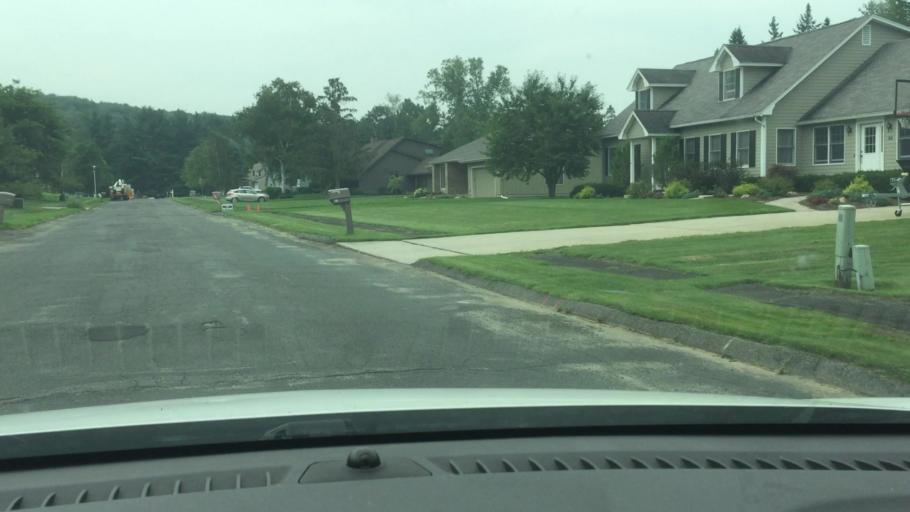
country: US
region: Massachusetts
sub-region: Berkshire County
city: Pittsfield
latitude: 42.4296
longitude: -73.2155
